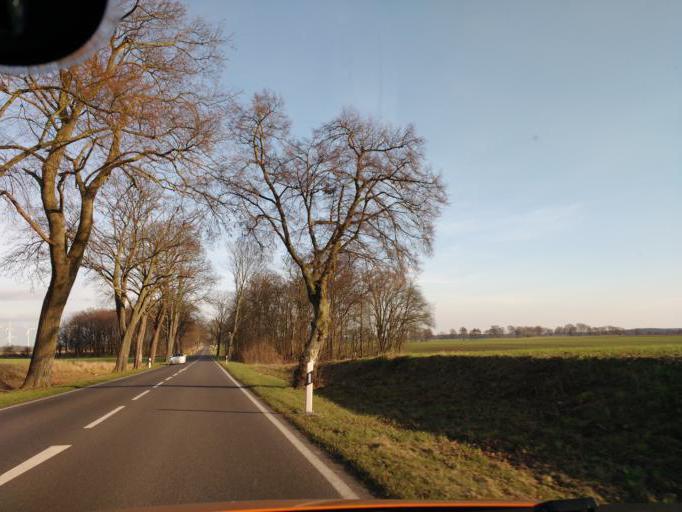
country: DE
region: Brandenburg
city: Protzel
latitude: 52.6589
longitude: 14.0383
